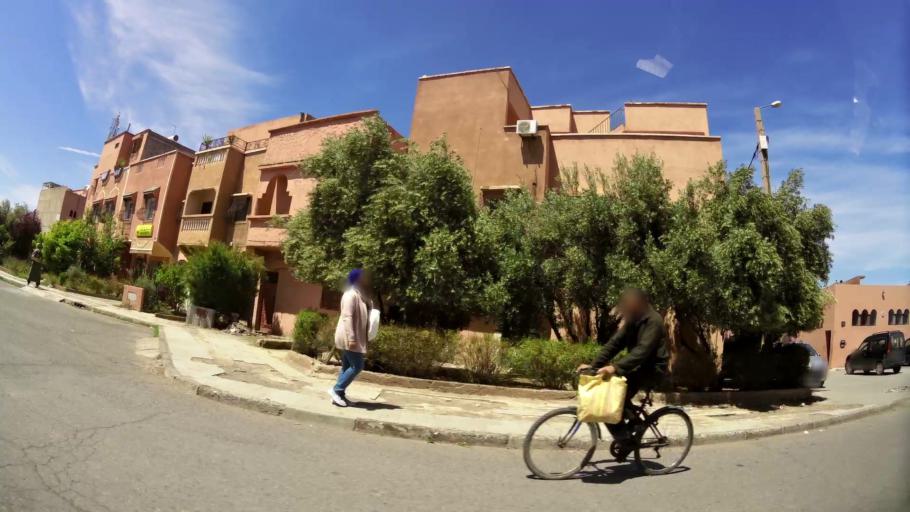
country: MA
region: Marrakech-Tensift-Al Haouz
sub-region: Marrakech
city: Marrakesh
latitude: 31.6384
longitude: -8.0536
